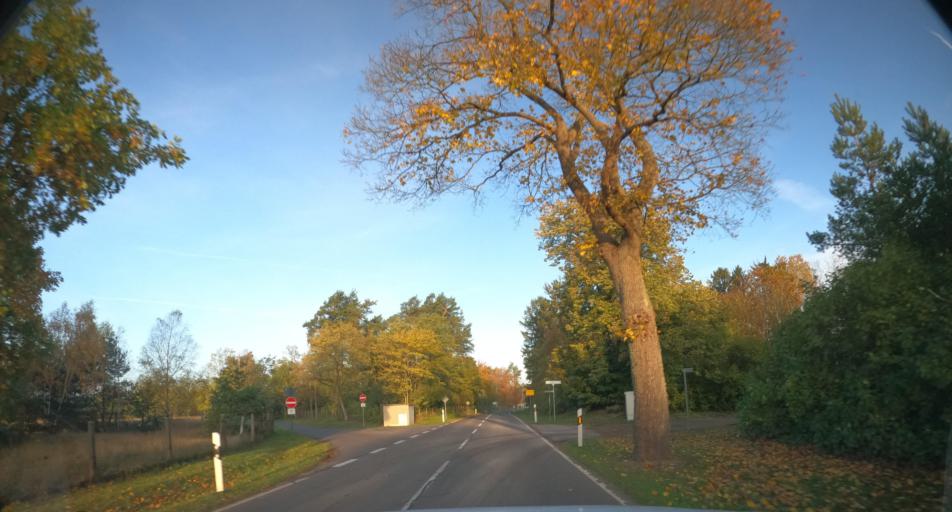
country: DE
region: Mecklenburg-Vorpommern
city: Ahlbeck
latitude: 53.6261
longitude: 14.2700
